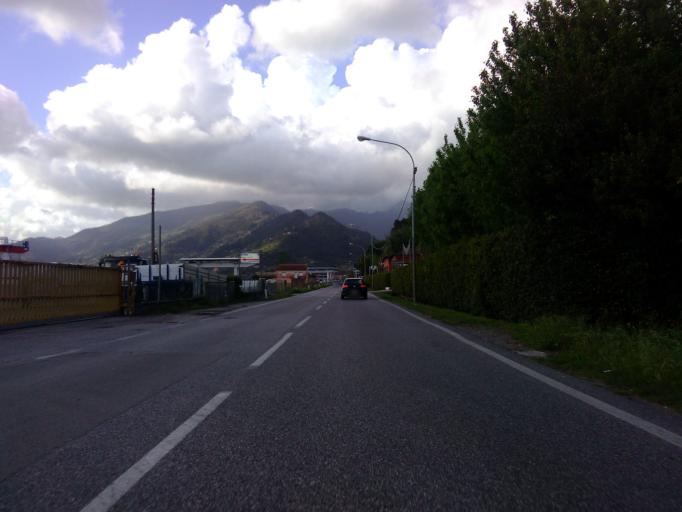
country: IT
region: Tuscany
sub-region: Provincia di Lucca
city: Ripa-Pozzi-Querceta-Ponterosso
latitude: 43.9700
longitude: 10.2206
